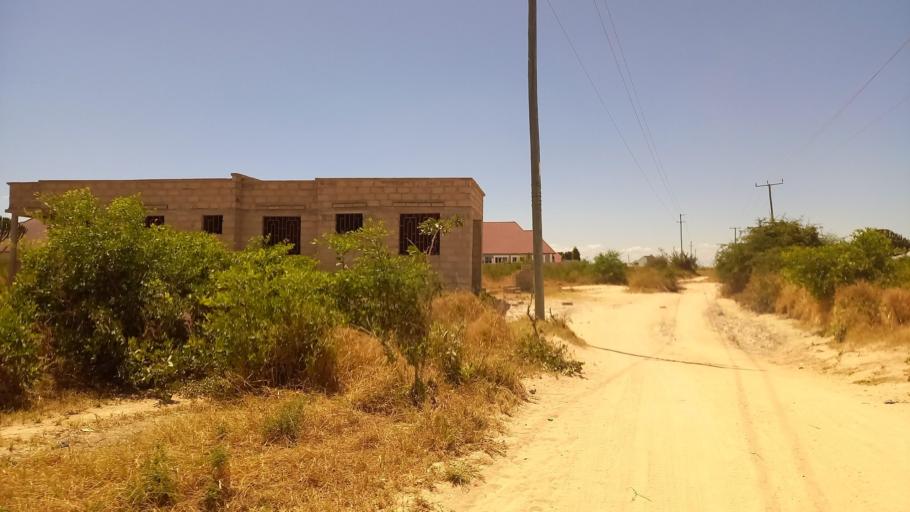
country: TZ
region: Dodoma
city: Dodoma
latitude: -6.1363
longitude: 35.7077
